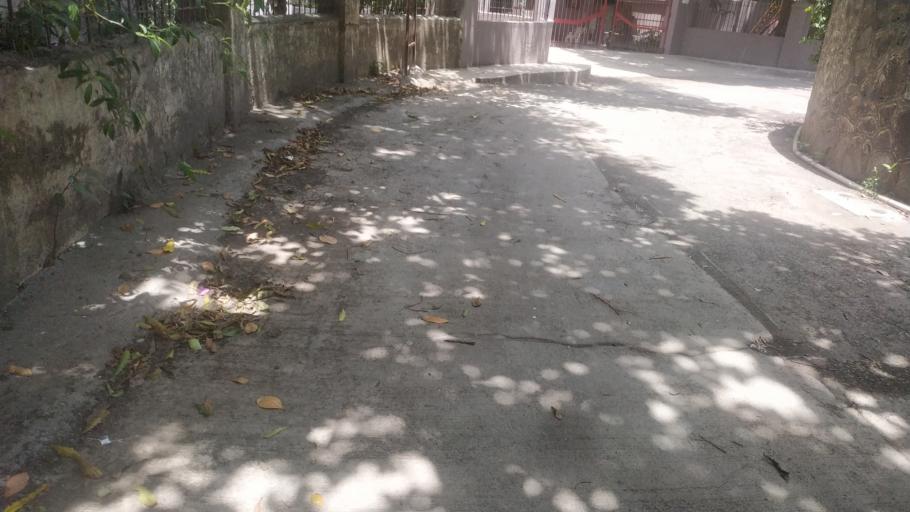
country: IN
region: Maharashtra
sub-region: Mumbai Suburban
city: Mumbai
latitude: 19.0536
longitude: 72.8687
